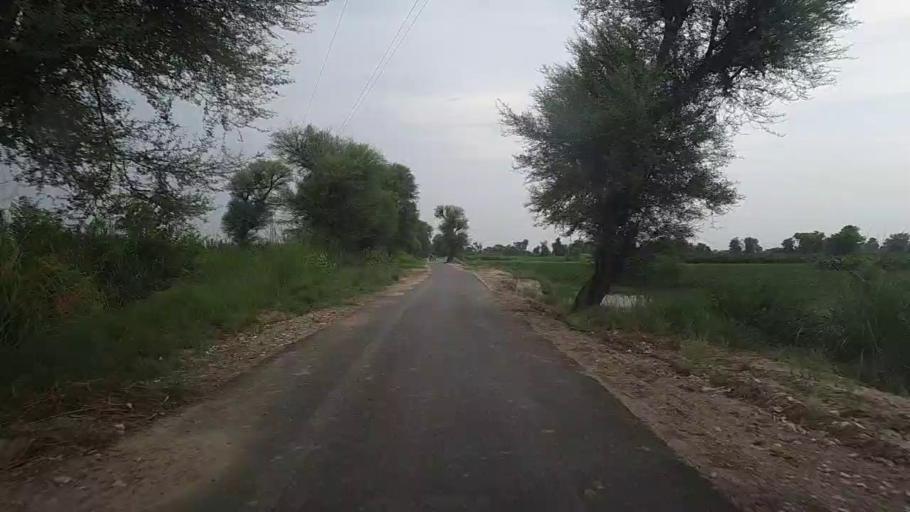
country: PK
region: Sindh
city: Karaundi
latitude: 26.9795
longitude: 68.3576
